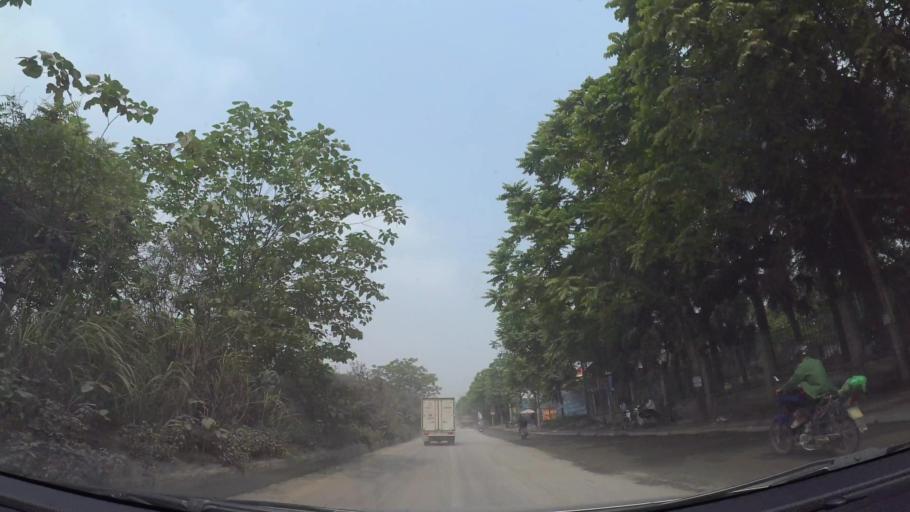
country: VN
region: Ha Noi
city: Cau Dien
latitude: 21.0112
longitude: 105.7288
